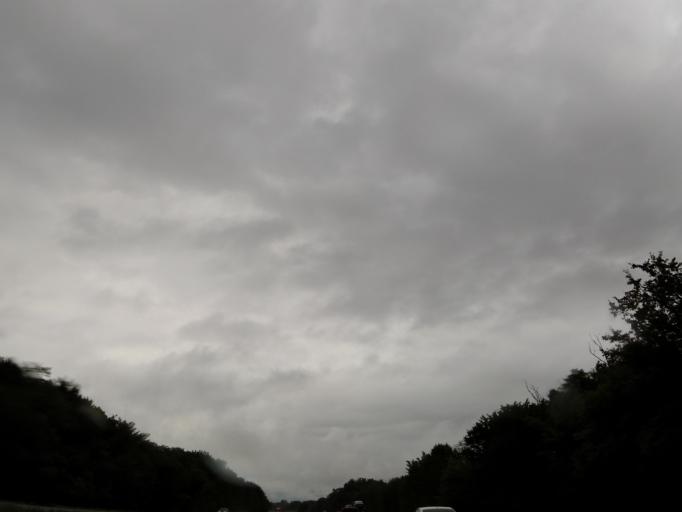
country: US
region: Illinois
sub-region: Jefferson County
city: Mount Vernon
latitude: 38.3557
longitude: -88.9963
